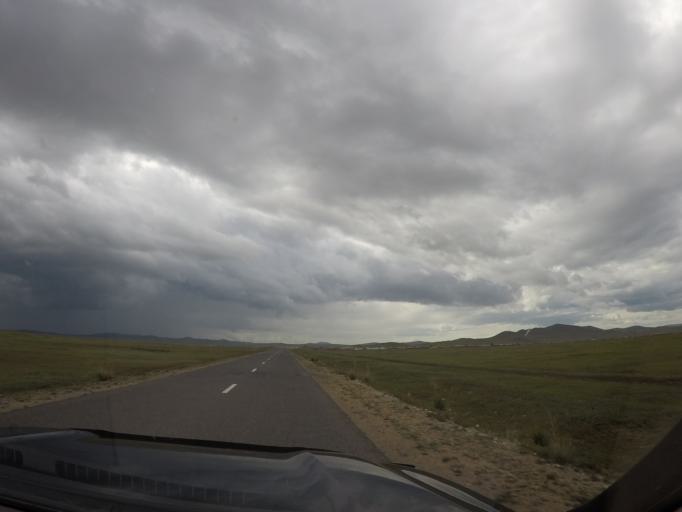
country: MN
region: Hentiy
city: Avraga
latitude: 47.4838
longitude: 109.4889
